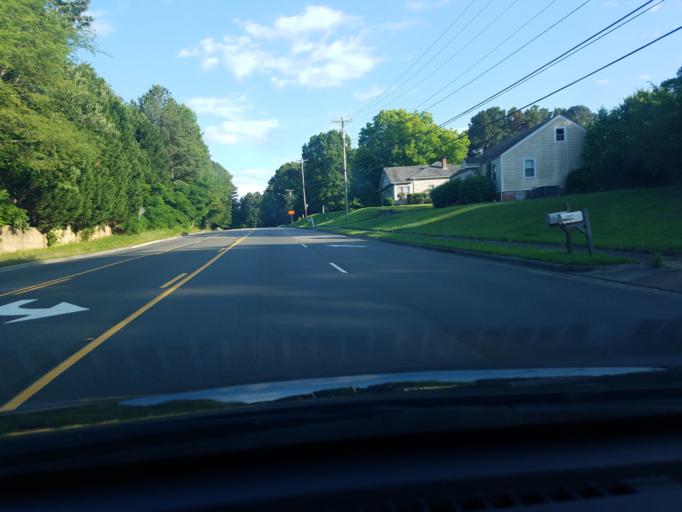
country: US
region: North Carolina
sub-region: Durham County
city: Durham
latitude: 35.9470
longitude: -78.9685
